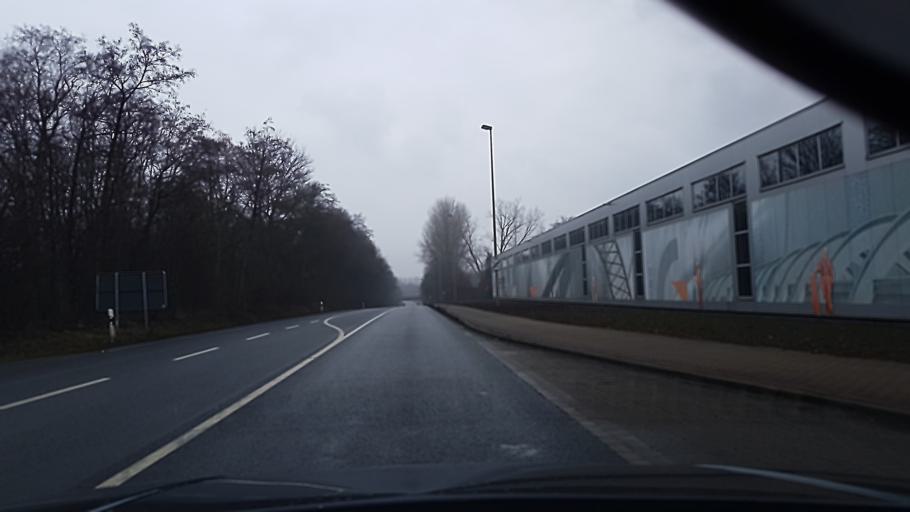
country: DE
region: Lower Saxony
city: Cramme
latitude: 52.1556
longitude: 10.4230
